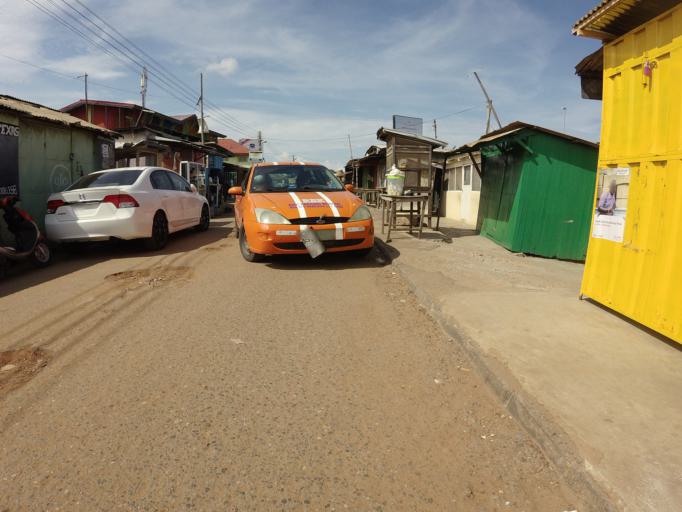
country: GH
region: Greater Accra
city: Accra
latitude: 5.5927
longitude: -0.1903
